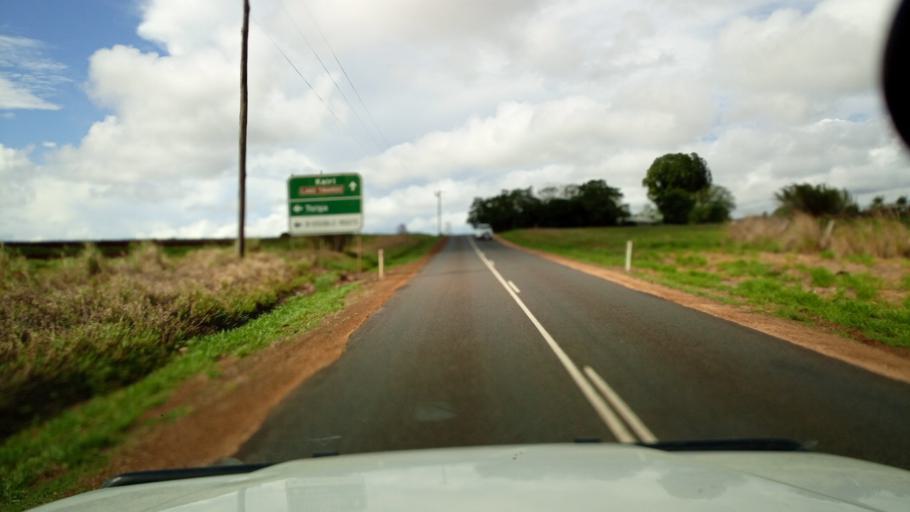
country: AU
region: Queensland
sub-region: Tablelands
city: Tolga
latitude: -17.2193
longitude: 145.5379
